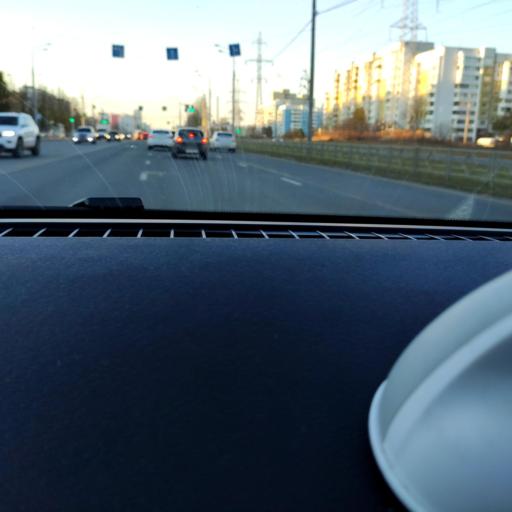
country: RU
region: Samara
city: Samara
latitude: 53.2656
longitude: 50.2193
